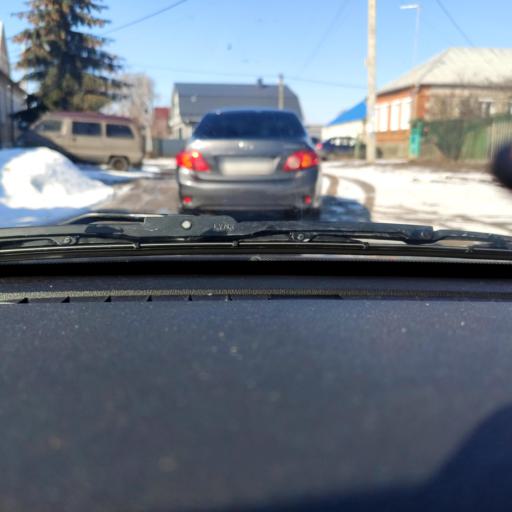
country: RU
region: Voronezj
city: Somovo
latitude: 51.7497
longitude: 39.3313
